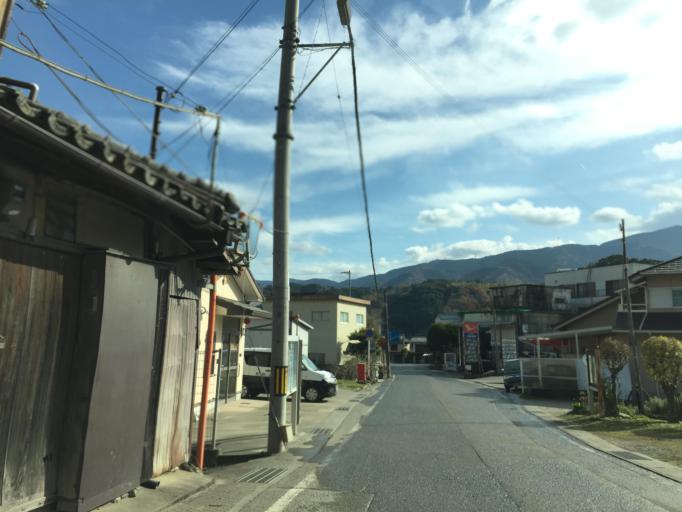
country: JP
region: Wakayama
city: Iwade
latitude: 34.1497
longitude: 135.3566
